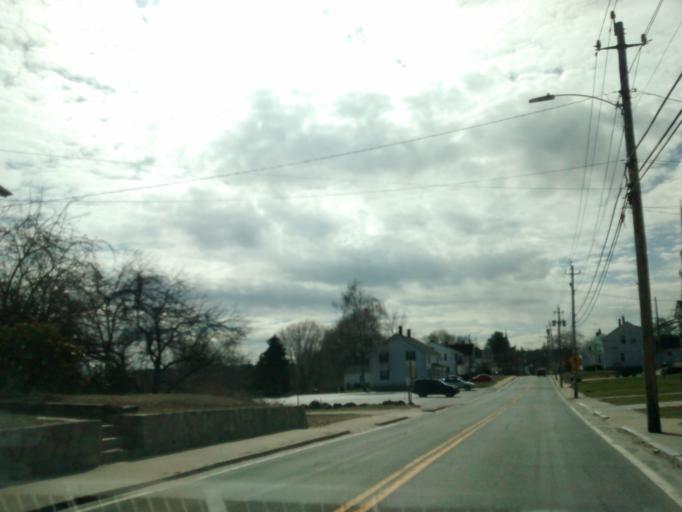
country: US
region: Rhode Island
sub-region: Providence County
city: Harrisville
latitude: 41.9685
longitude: -71.6782
